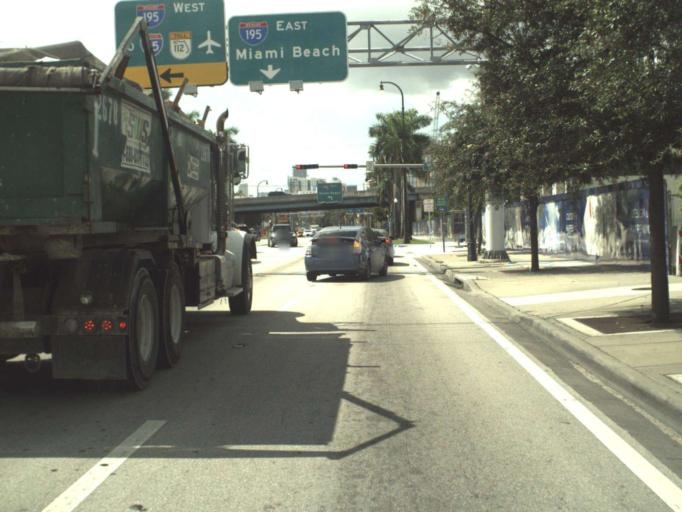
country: US
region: Florida
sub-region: Miami-Dade County
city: Allapattah
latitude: 25.8131
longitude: -80.1893
